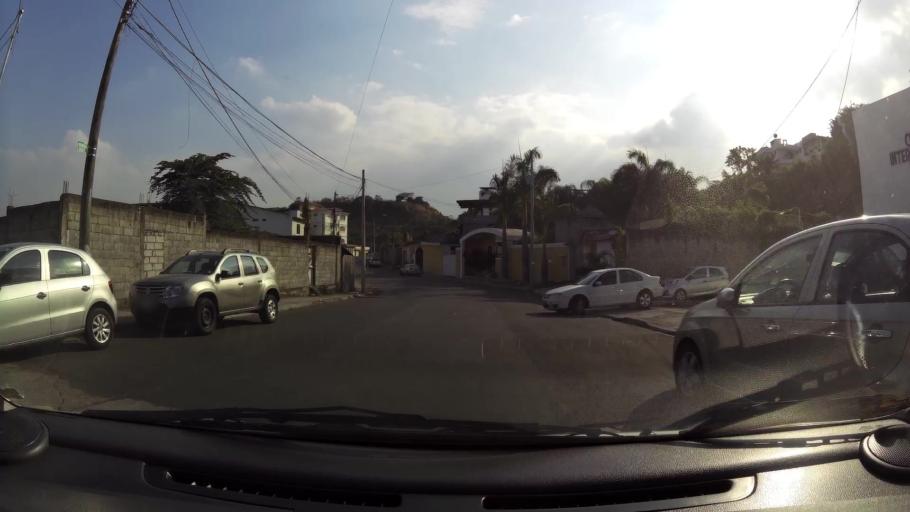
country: EC
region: Guayas
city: Guayaquil
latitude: -2.1564
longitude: -79.9061
